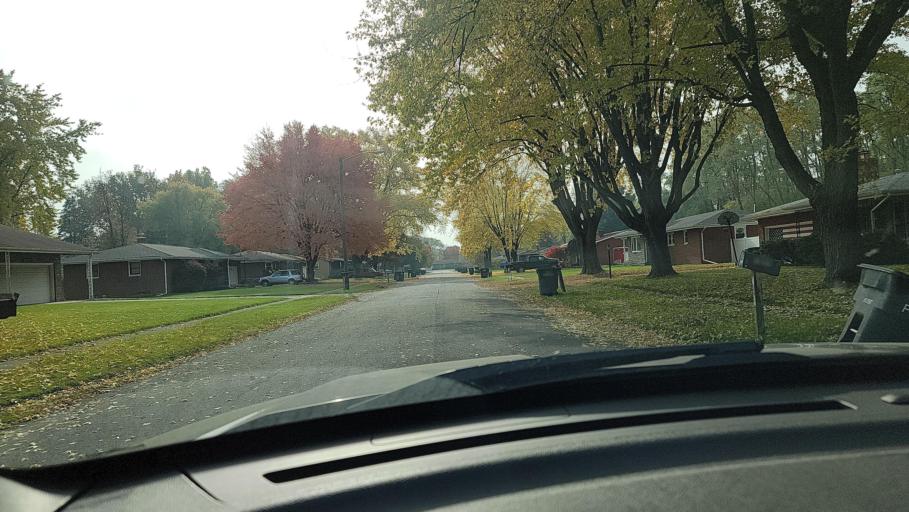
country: US
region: Indiana
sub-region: Porter County
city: Portage
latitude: 41.5965
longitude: -87.1677
